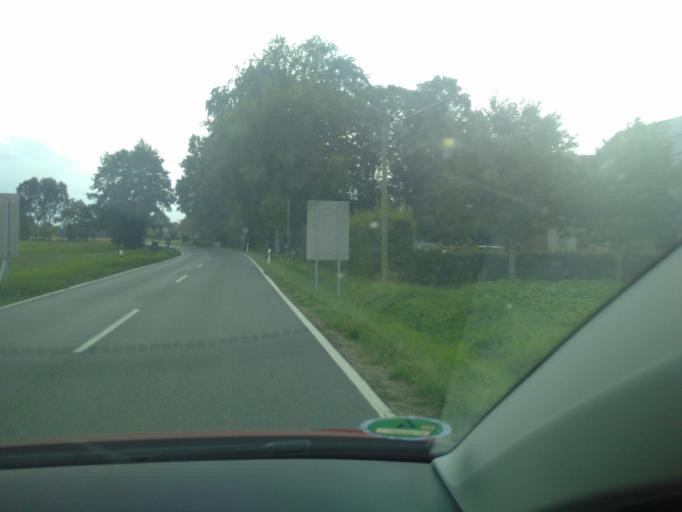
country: DE
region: North Rhine-Westphalia
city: Borgholzhausen
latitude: 52.0564
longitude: 8.2517
